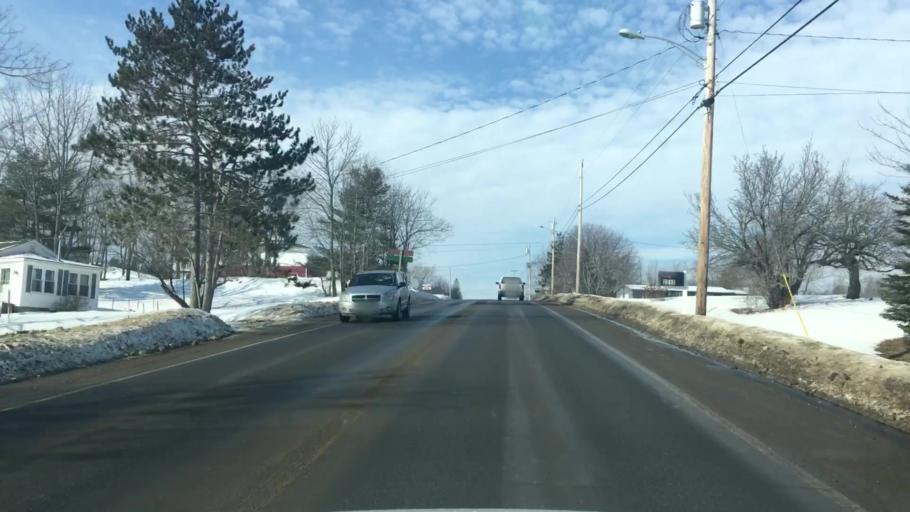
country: US
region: Maine
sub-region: Penobscot County
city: Hermon
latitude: 44.8450
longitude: -68.8675
